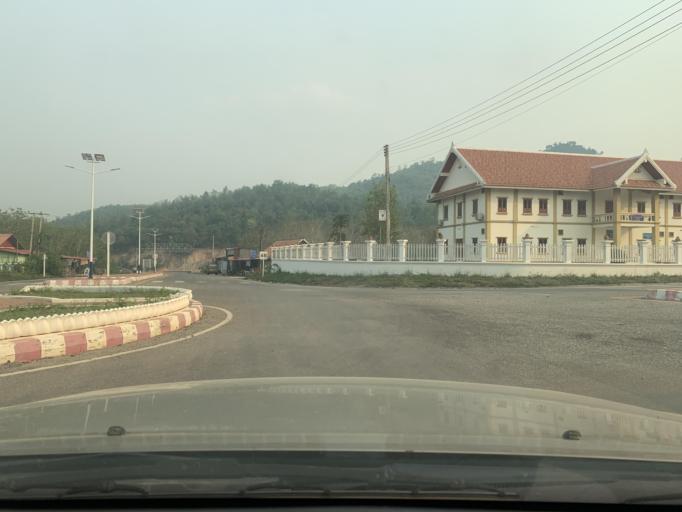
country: LA
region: Louangphabang
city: Louangphabang
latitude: 19.9071
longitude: 102.0852
